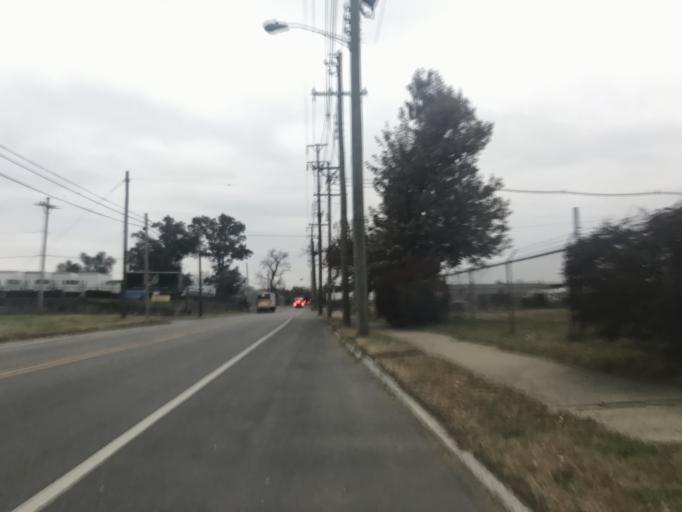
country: US
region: Kentucky
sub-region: Jefferson County
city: Louisville
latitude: 38.2321
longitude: -85.7744
